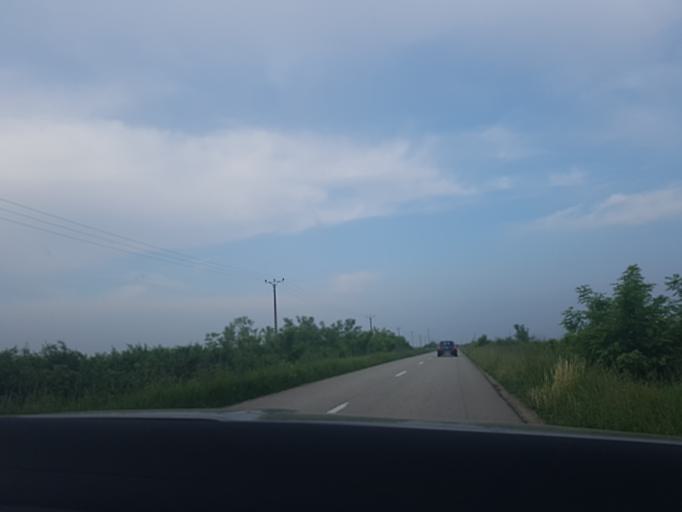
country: RO
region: Timis
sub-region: Comuna Foeni
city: Foeni
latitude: 45.5206
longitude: 20.9101
